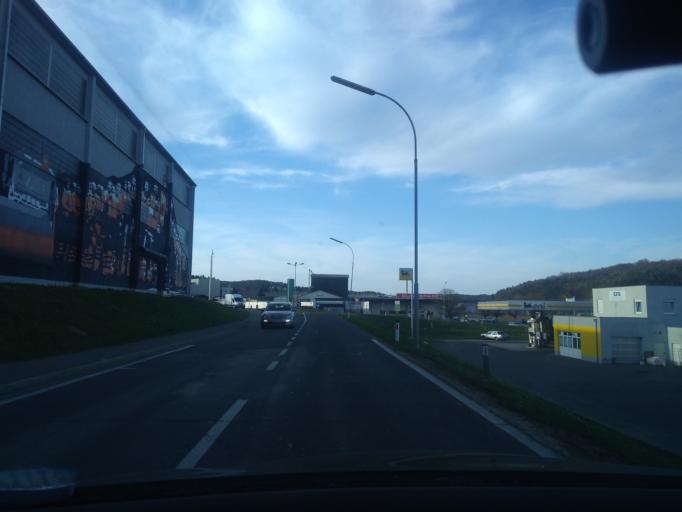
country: AT
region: Styria
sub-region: Politischer Bezirk Suedoststeiermark
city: Sankt Stefan im Rosental
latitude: 46.9006
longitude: 15.7133
